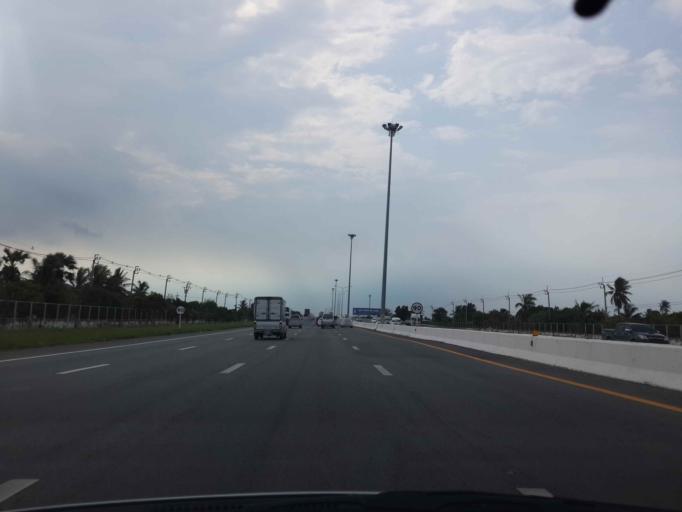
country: TH
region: Samut Prakan
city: Ban Khlong Bang Sao Thong
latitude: 13.6282
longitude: 100.9088
